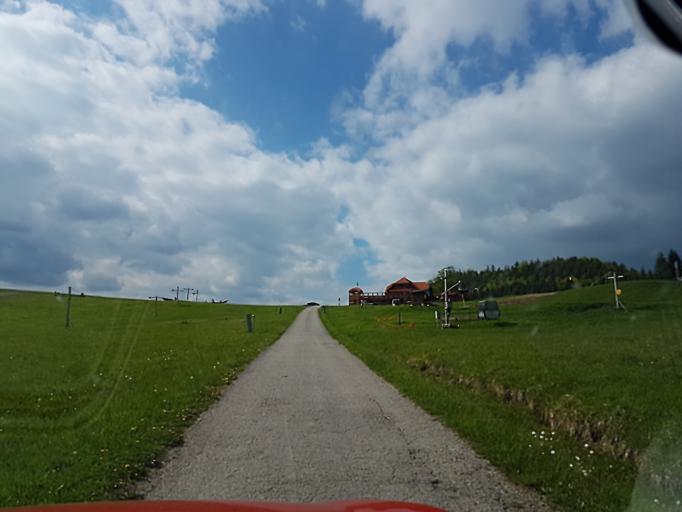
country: SK
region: Zilinsky
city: Ruzomberok
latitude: 49.0519
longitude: 19.2647
